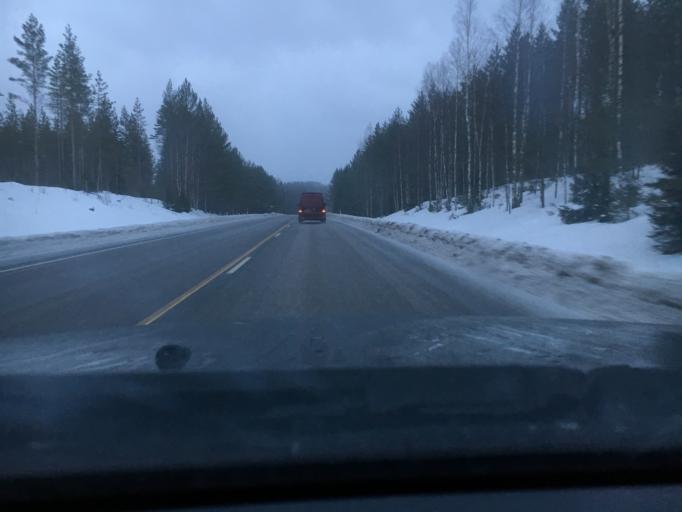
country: FI
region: Central Finland
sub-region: Jyvaeskylae
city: Hankasalmi
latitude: 62.4111
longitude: 26.6891
